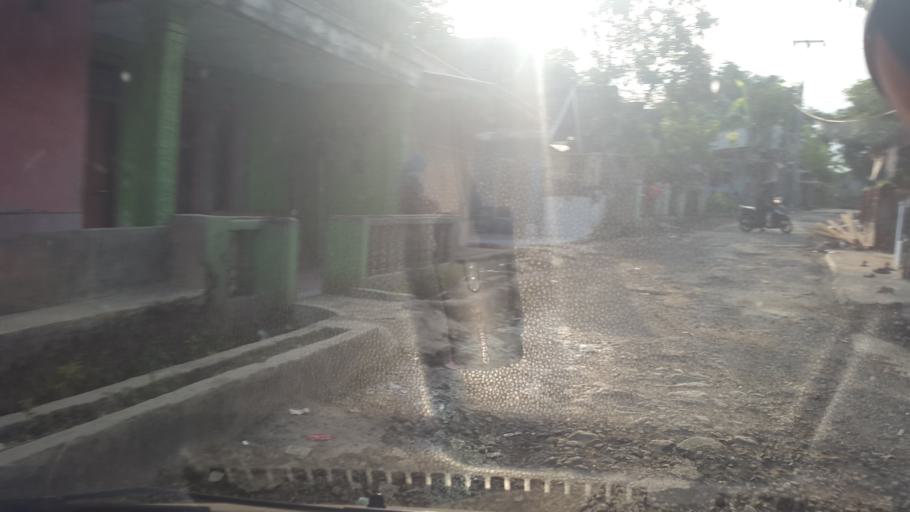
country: ID
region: West Java
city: Cicurug
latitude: -6.8201
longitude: 106.7482
